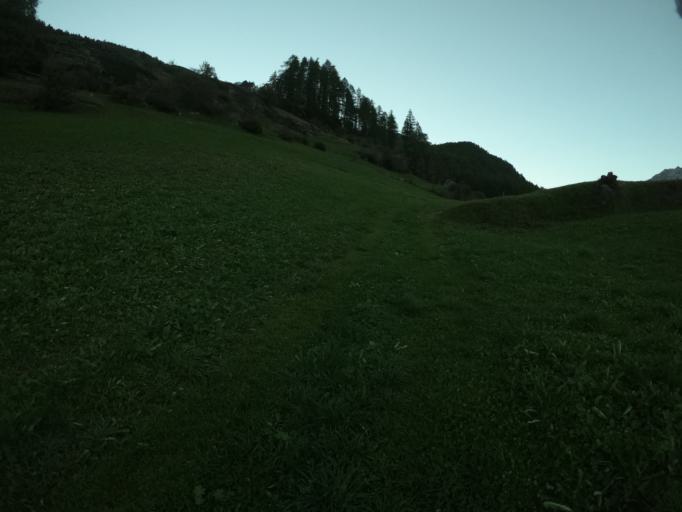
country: AT
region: Tyrol
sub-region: Politischer Bezirk Imst
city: Soelden
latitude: 46.9632
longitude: 11.0126
